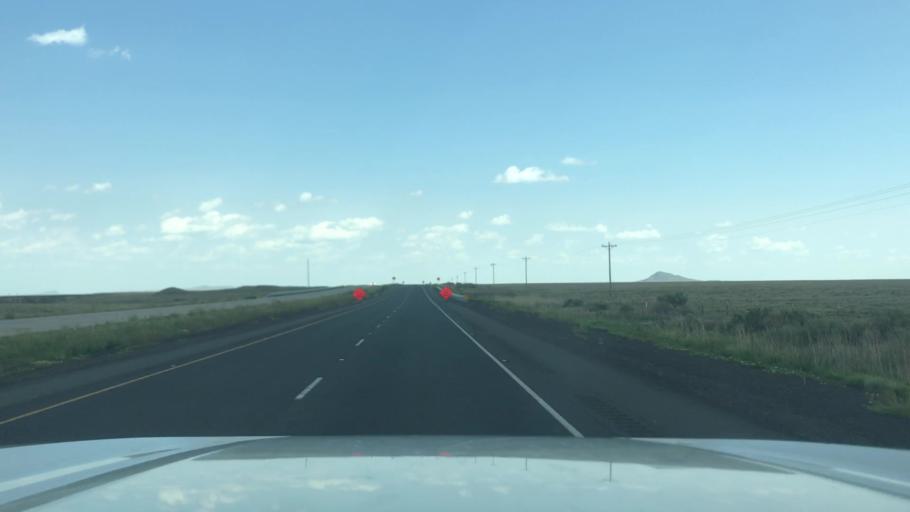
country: US
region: New Mexico
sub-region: Union County
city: Clayton
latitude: 36.6258
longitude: -103.7045
